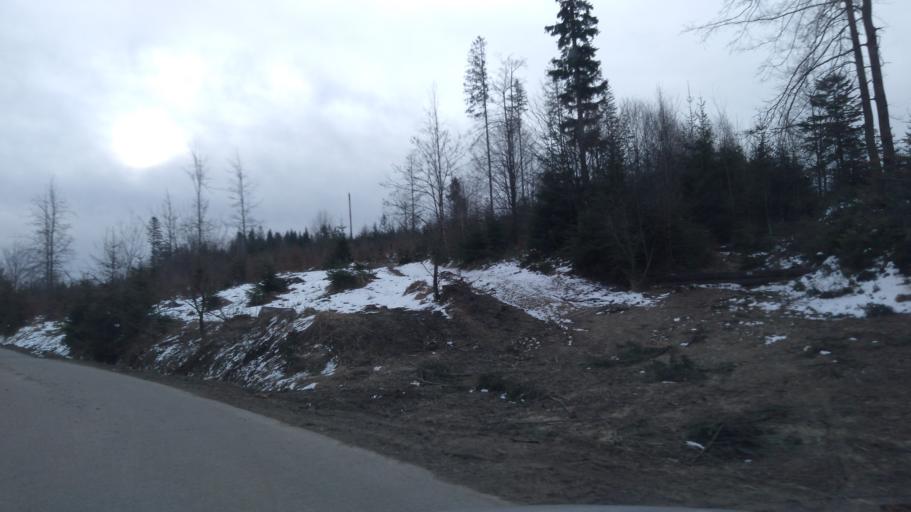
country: PL
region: Silesian Voivodeship
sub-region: Powiat cieszynski
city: Koniakow
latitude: 49.5301
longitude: 18.9510
